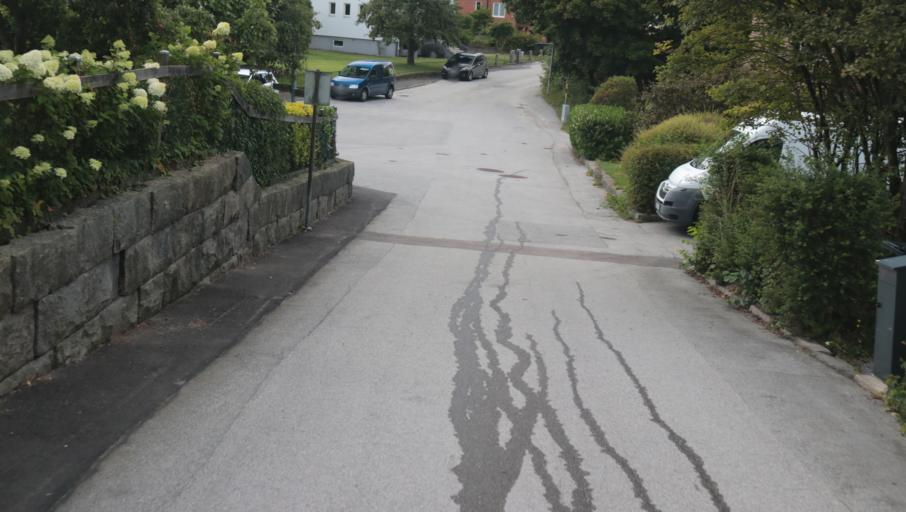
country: SE
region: Blekinge
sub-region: Karlshamns Kommun
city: Karlshamn
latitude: 56.1710
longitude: 14.8730
